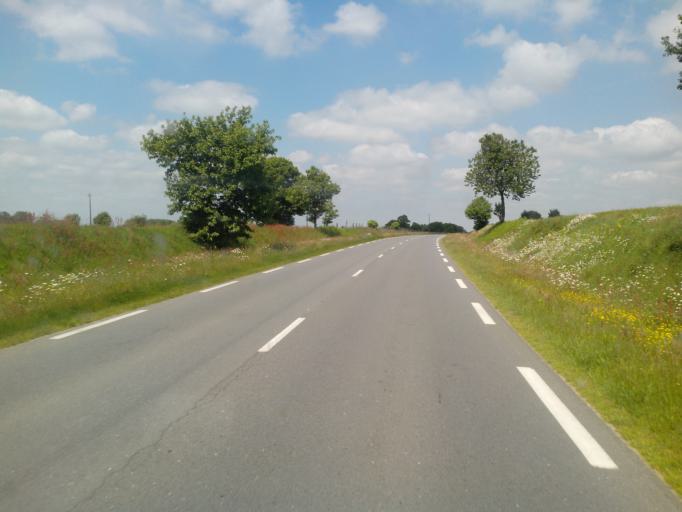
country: FR
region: Brittany
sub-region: Departement d'Ille-et-Vilaine
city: Saint-Germain-en-Cogles
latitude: 48.3823
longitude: -1.2674
